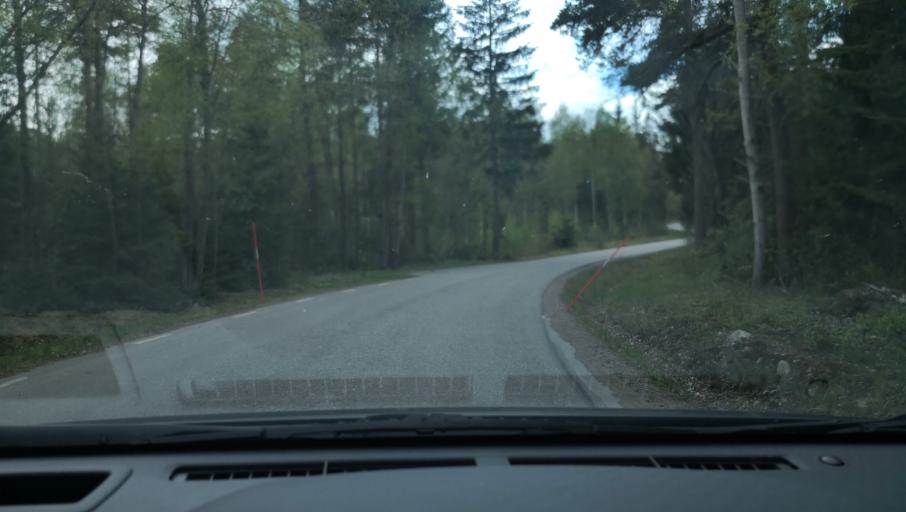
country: SE
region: OErebro
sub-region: Kumla Kommun
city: Hallabrottet
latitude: 59.1563
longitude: 15.1953
